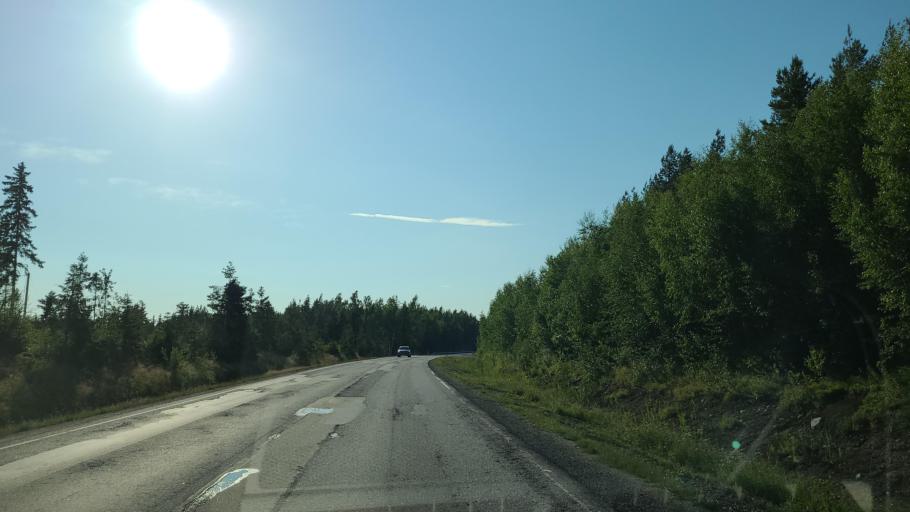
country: FI
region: Ostrobothnia
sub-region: Vaasa
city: Replot
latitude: 63.2082
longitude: 21.4406
